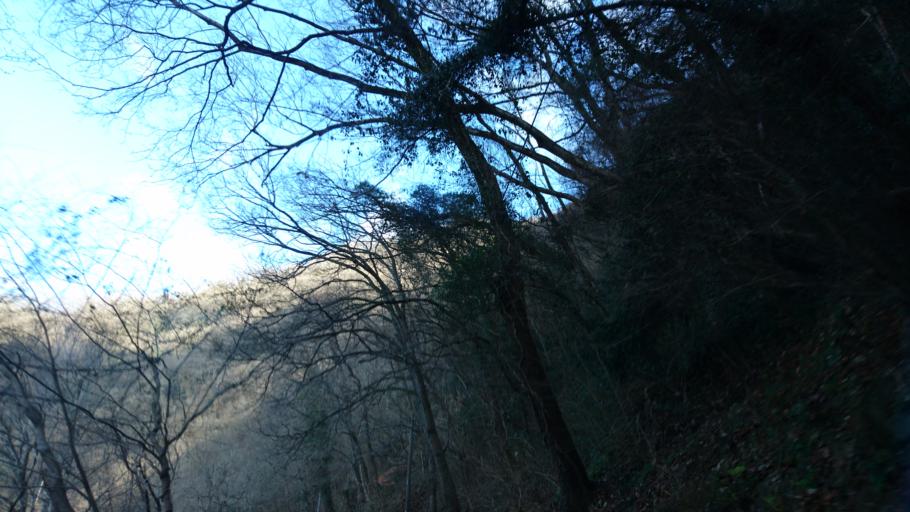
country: JP
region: Okayama
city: Takahashi
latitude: 34.8582
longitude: 133.5725
